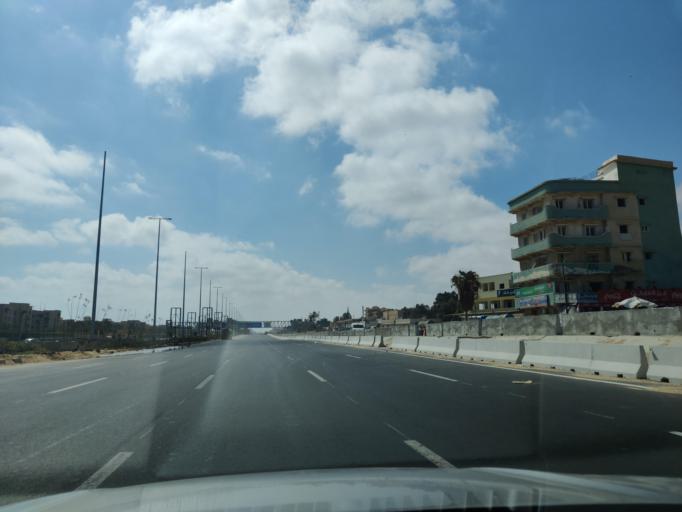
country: EG
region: Muhafazat Matruh
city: Al `Alamayn
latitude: 30.9711
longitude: 28.7385
